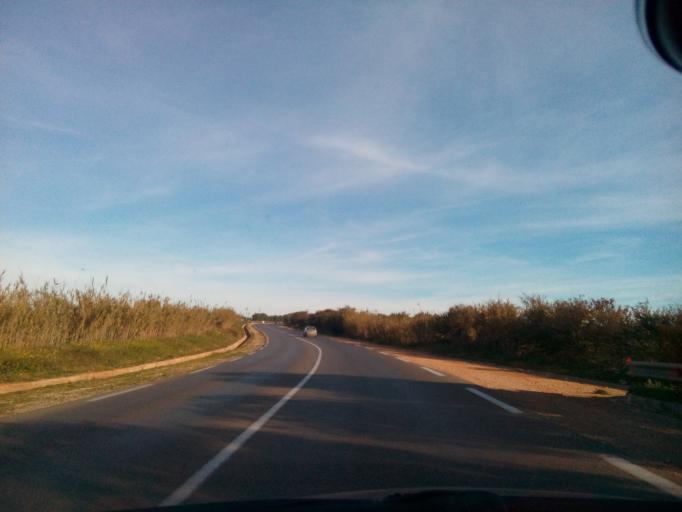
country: DZ
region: Mostaganem
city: Mostaganem
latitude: 35.8492
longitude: 0.1648
